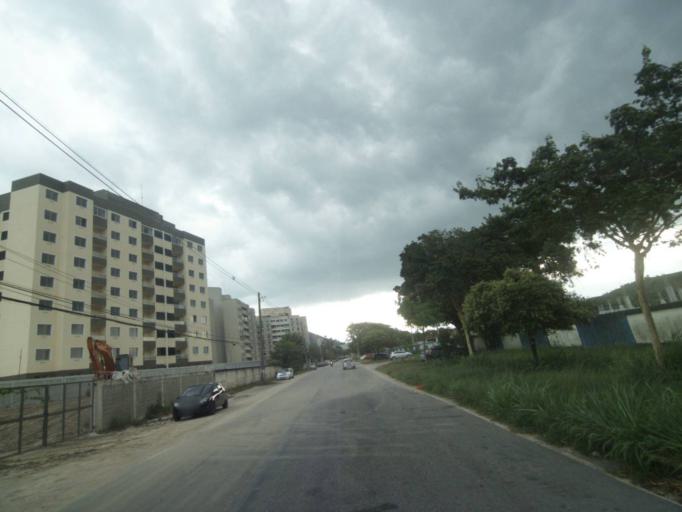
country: BR
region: Rio de Janeiro
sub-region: Nilopolis
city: Nilopolis
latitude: -22.8852
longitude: -43.3941
